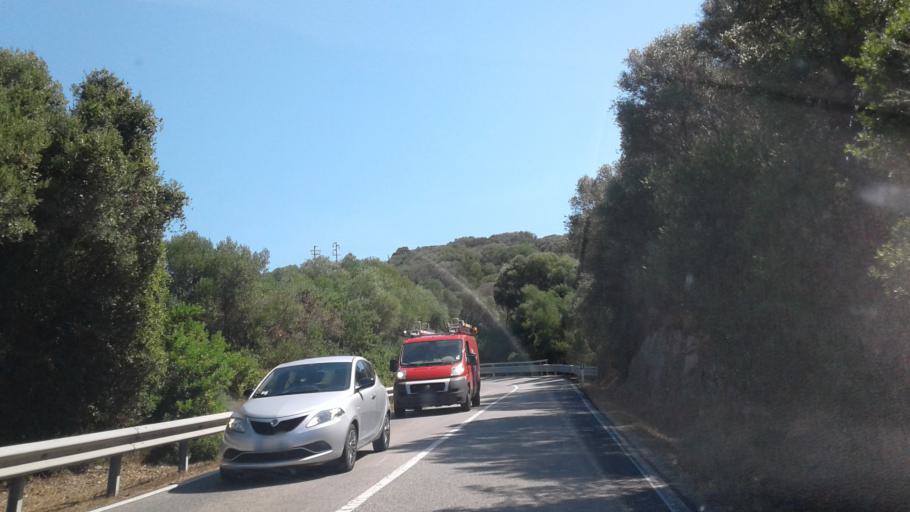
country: IT
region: Sardinia
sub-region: Provincia di Olbia-Tempio
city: Palau
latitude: 41.1672
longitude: 9.3168
